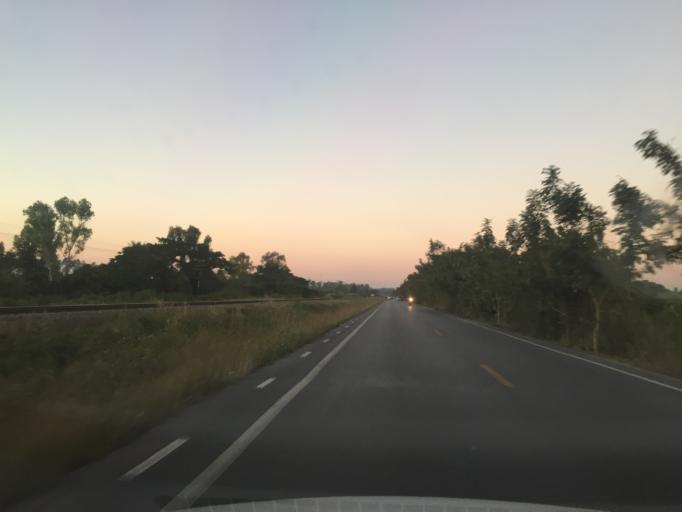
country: TH
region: Chiang Mai
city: Saraphi
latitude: 18.6615
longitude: 99.0446
